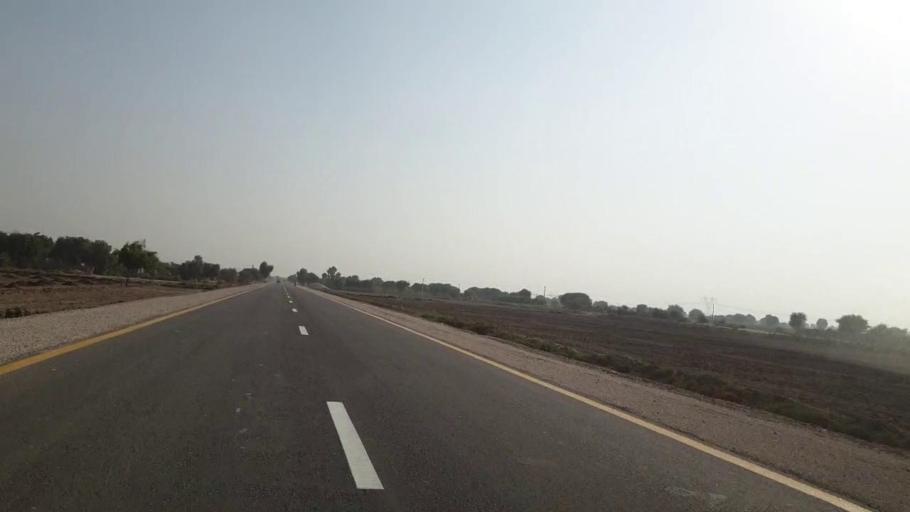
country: PK
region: Sindh
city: Bhan
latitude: 26.4913
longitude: 67.7799
